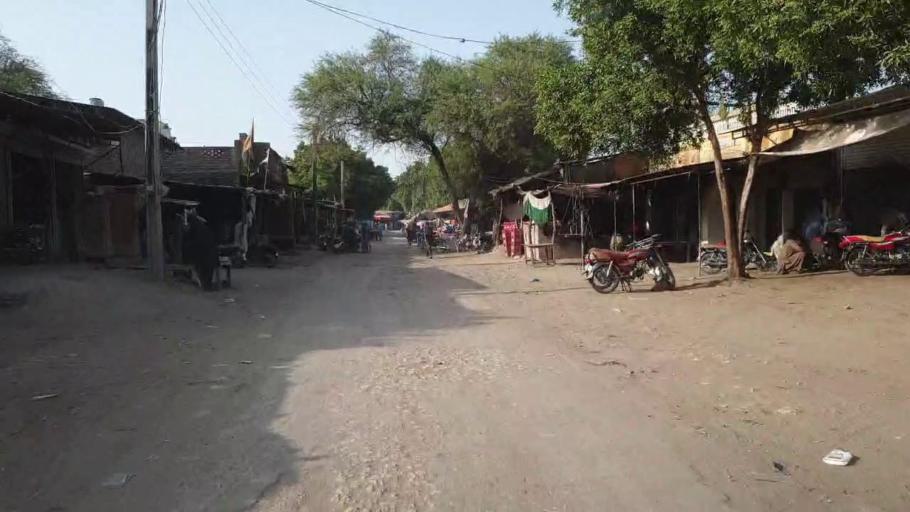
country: PK
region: Sindh
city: Jam Sahib
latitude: 26.4271
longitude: 68.8728
